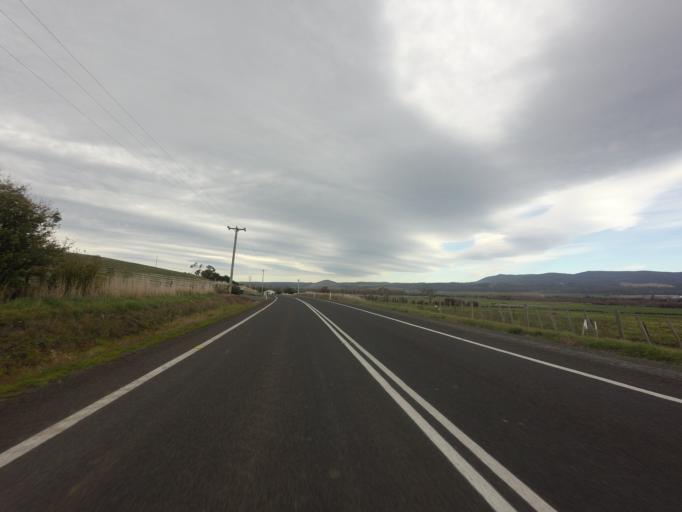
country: AU
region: Tasmania
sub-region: Derwent Valley
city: New Norfolk
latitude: -42.4958
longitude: 146.7297
